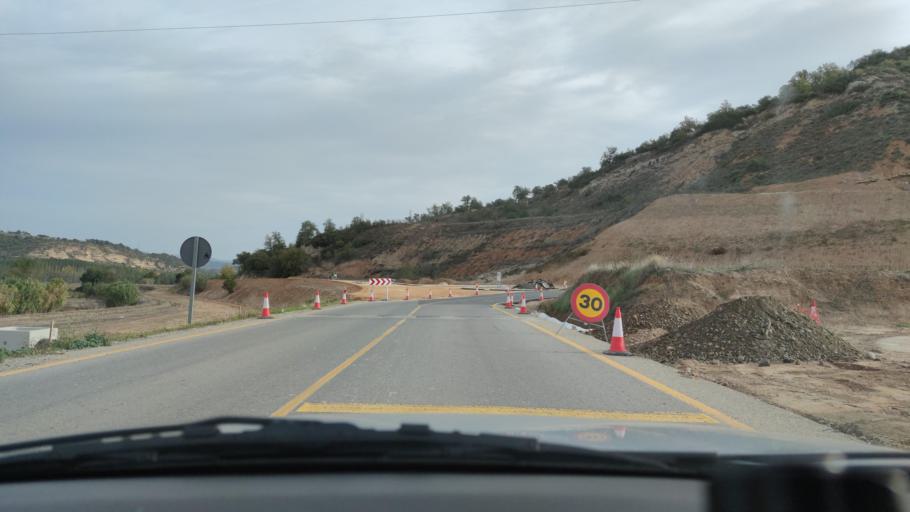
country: ES
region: Catalonia
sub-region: Provincia de Lleida
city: Artesa de Segre
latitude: 41.8974
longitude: 1.0590
